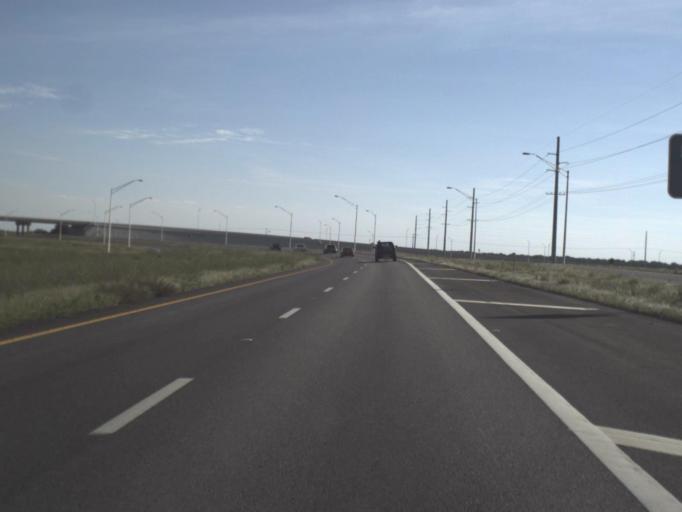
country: US
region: Florida
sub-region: Glades County
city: Moore Haven
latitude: 26.7591
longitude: -81.0832
